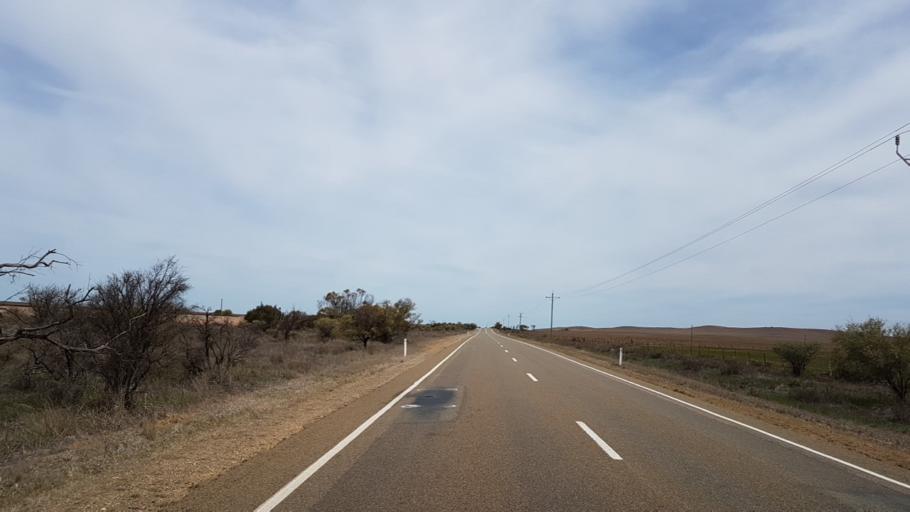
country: AU
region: South Australia
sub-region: Peterborough
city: Peterborough
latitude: -33.0071
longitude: 138.7695
